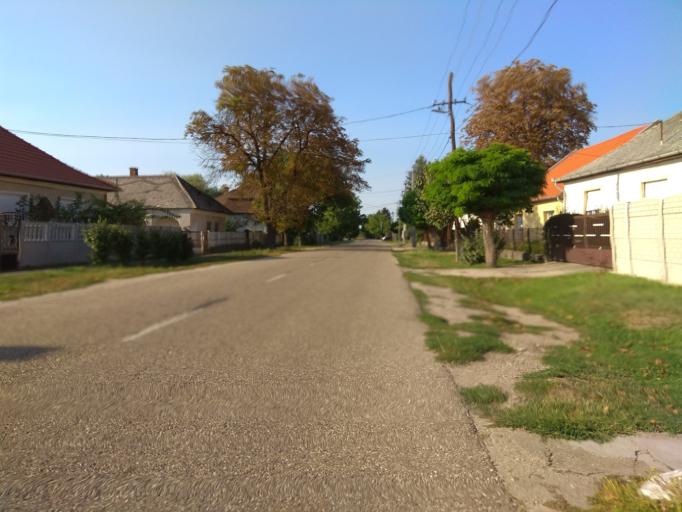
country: HU
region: Borsod-Abauj-Zemplen
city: Onod
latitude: 47.9646
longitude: 20.8837
